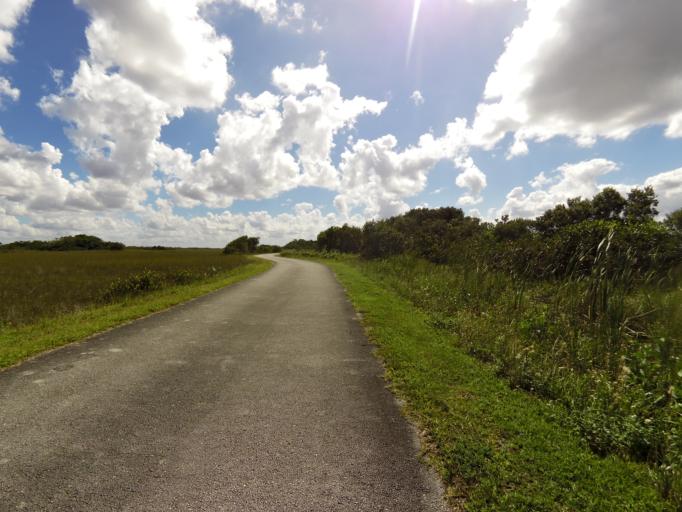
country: US
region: Florida
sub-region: Miami-Dade County
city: The Hammocks
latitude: 25.7282
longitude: -80.7667
